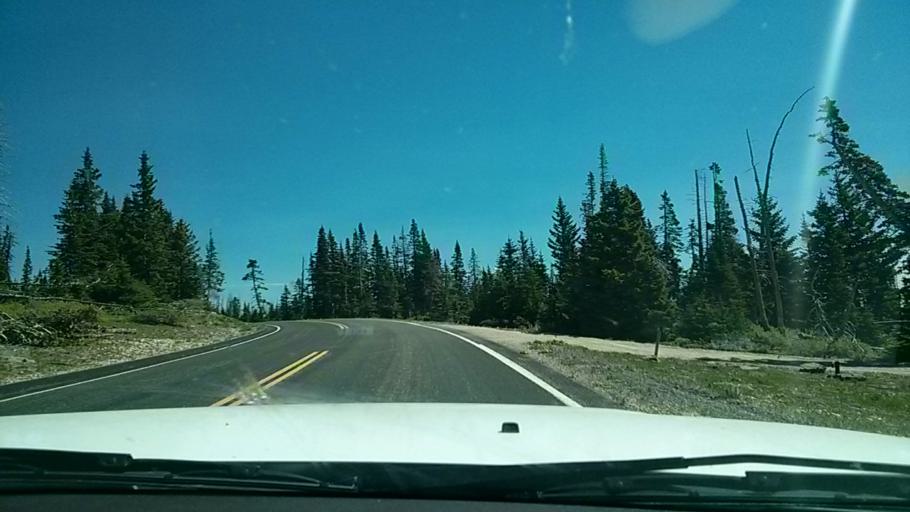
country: US
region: Utah
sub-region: Iron County
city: Parowan
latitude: 37.6347
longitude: -112.8230
